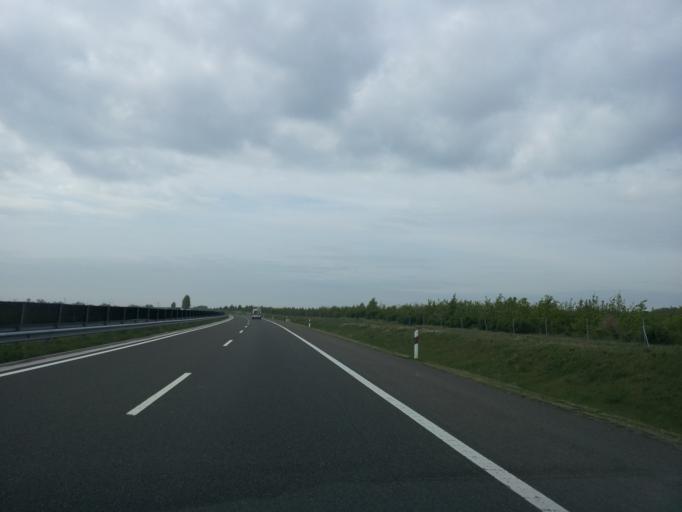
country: HU
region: Fejer
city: Baracs
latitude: 46.8895
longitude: 18.8758
